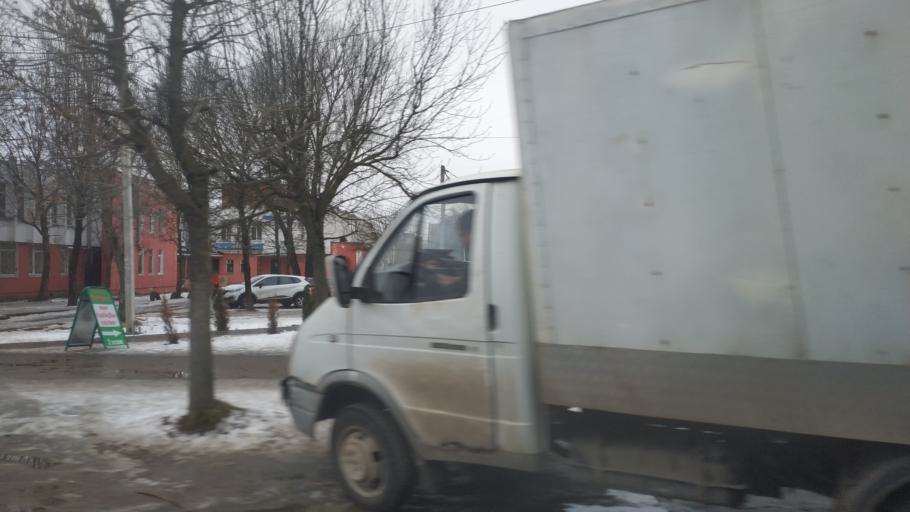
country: RU
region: Tverskaya
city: Tver
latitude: 56.8841
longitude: 35.8402
